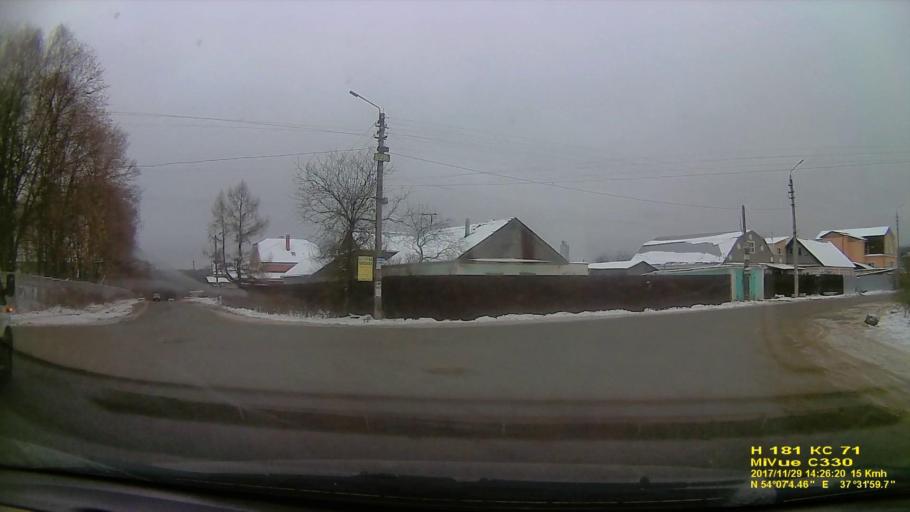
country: RU
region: Tula
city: Kosaya Gora
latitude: 54.1179
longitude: 37.5333
